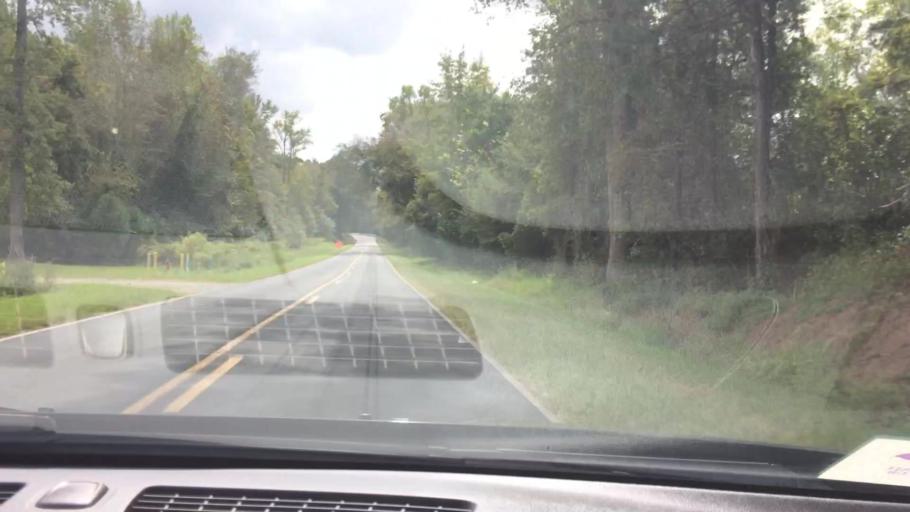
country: US
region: North Carolina
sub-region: Greene County
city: Maury
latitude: 35.5363
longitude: -77.5451
